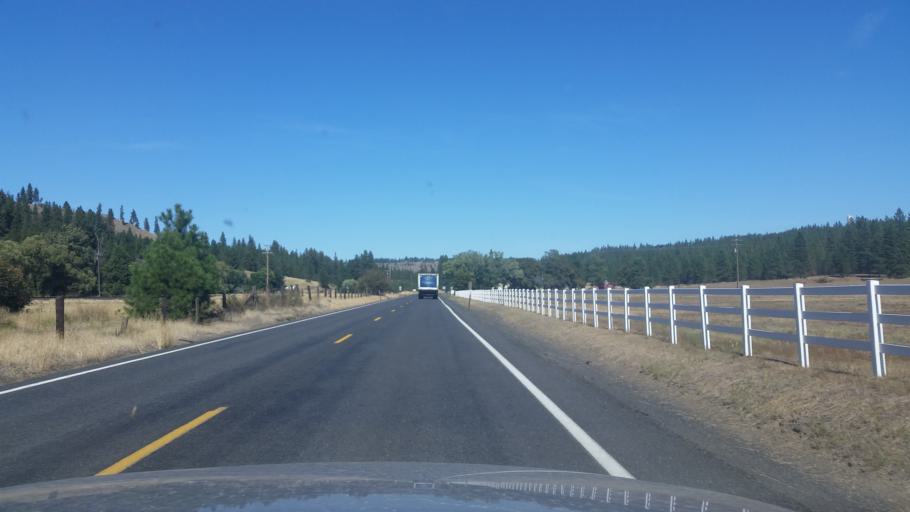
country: US
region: Washington
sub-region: Spokane County
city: Spokane
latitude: 47.5917
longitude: -117.4497
